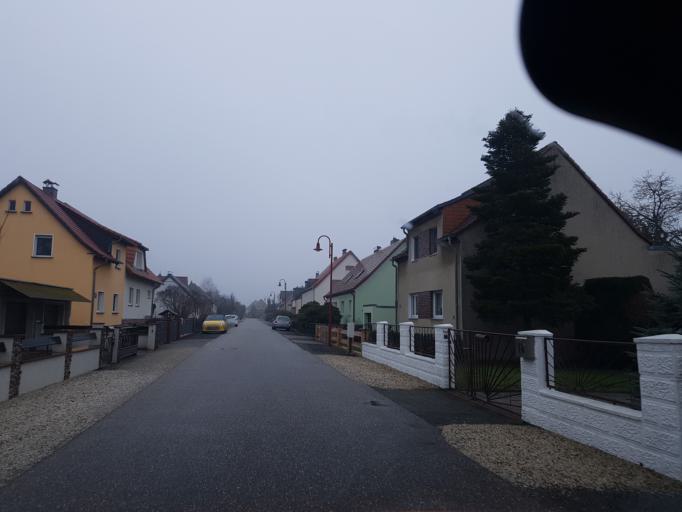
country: DE
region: Brandenburg
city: Finsterwalde
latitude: 51.6493
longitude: 13.6981
